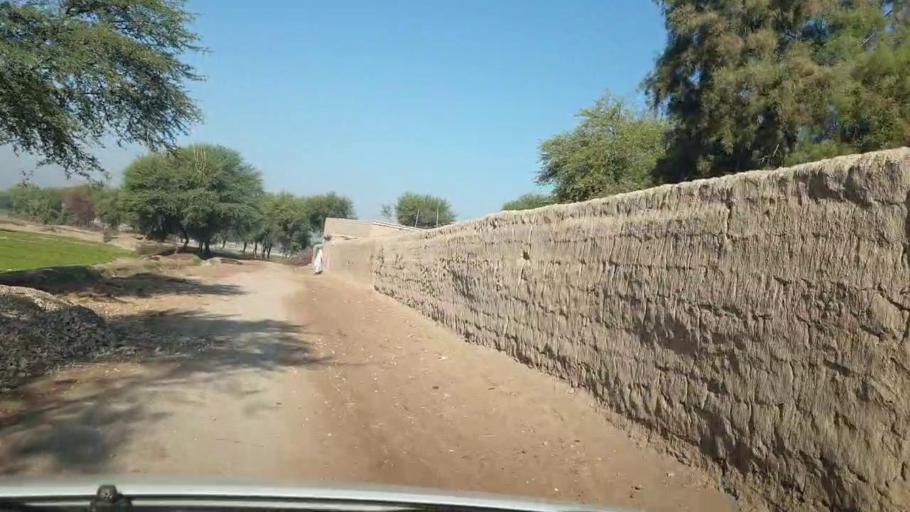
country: PK
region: Sindh
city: Dadu
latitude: 26.6745
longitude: 67.8387
